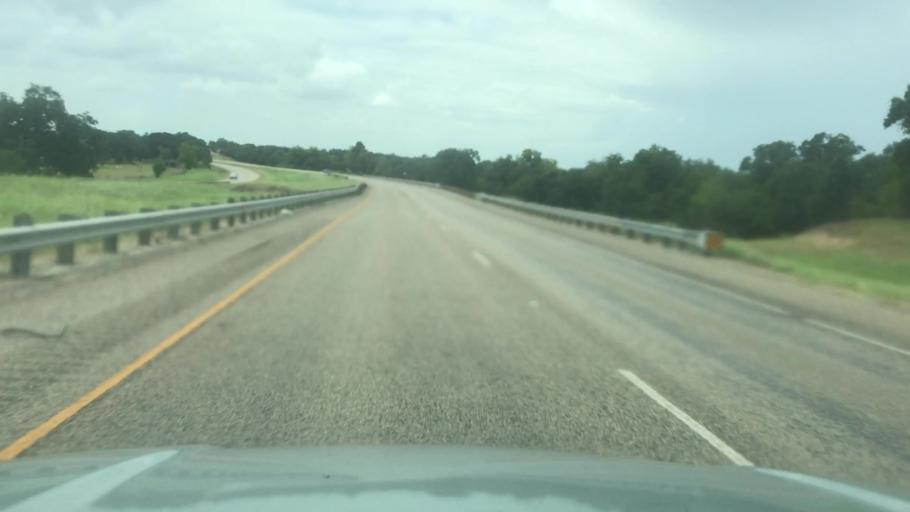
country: US
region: Texas
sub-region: Fayette County
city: La Grange
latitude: 29.8973
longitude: -96.7749
